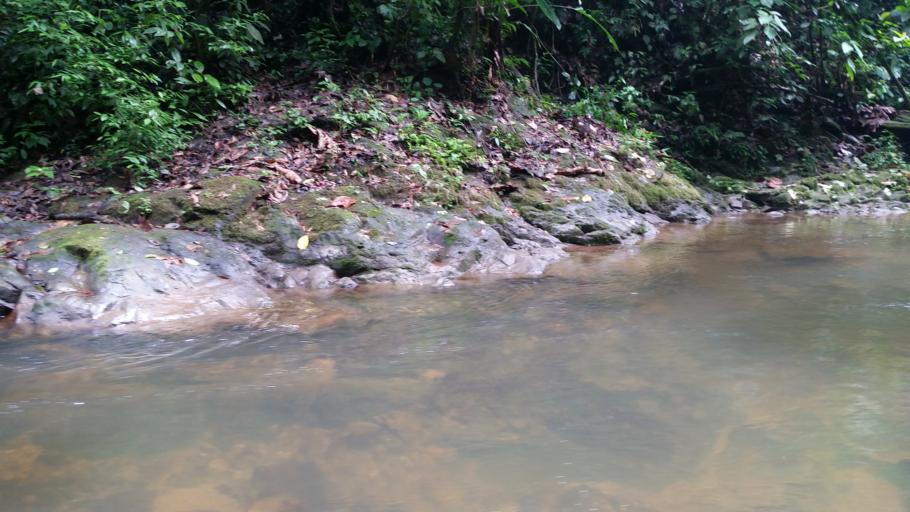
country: NI
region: Atlantico Norte (RAAN)
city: Bonanza
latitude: 14.0256
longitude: -84.7488
